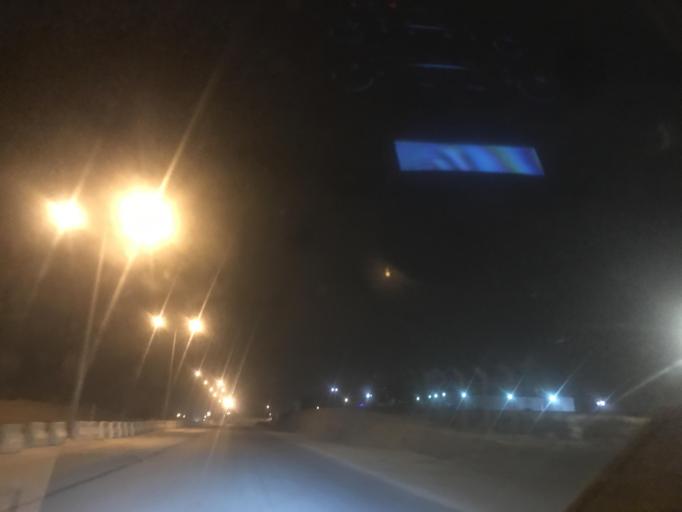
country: SA
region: Ar Riyad
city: Riyadh
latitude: 24.7597
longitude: 46.5895
